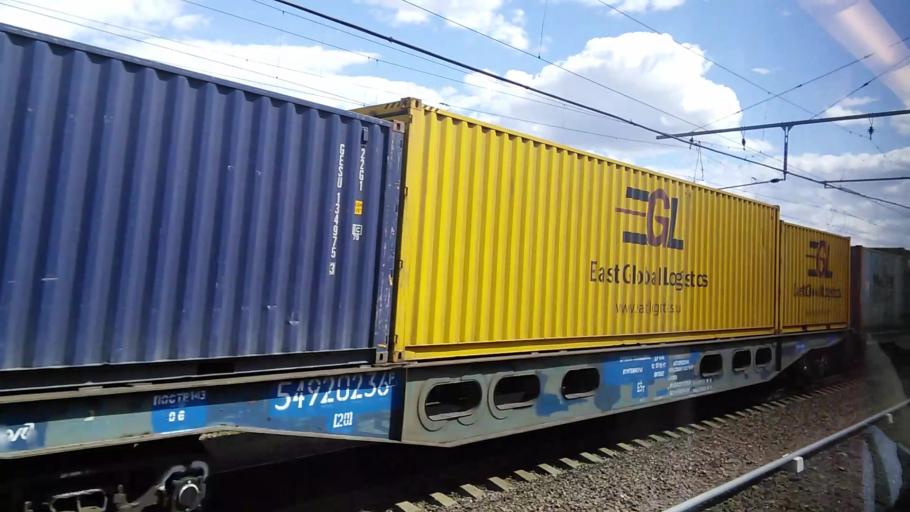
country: RU
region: Moscow
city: Mar'ina Roshcha
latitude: 55.8028
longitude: 37.5882
